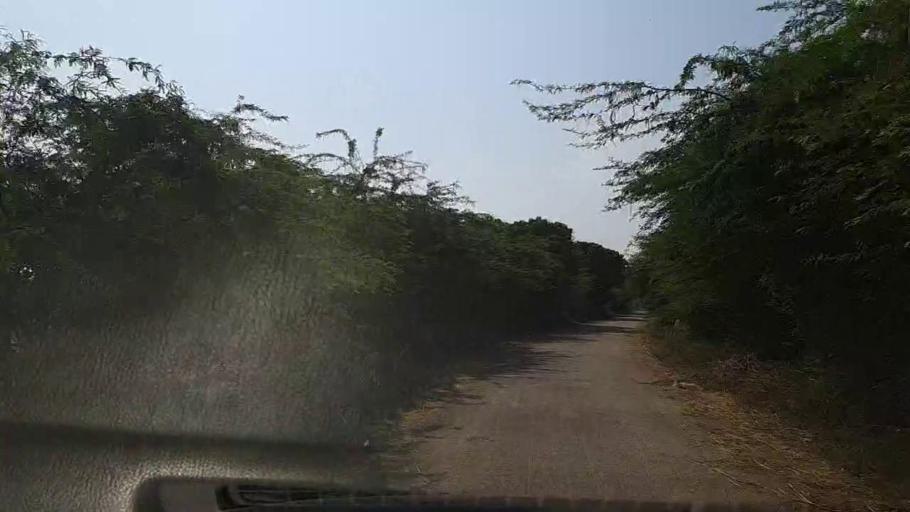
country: PK
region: Sindh
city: Thatta
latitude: 24.8040
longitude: 67.8444
